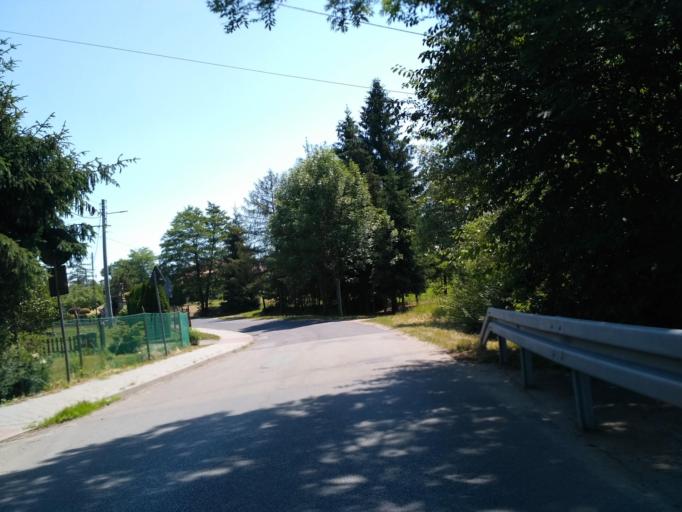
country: PL
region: Subcarpathian Voivodeship
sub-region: Krosno
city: Krosno
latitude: 49.6955
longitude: 21.7873
